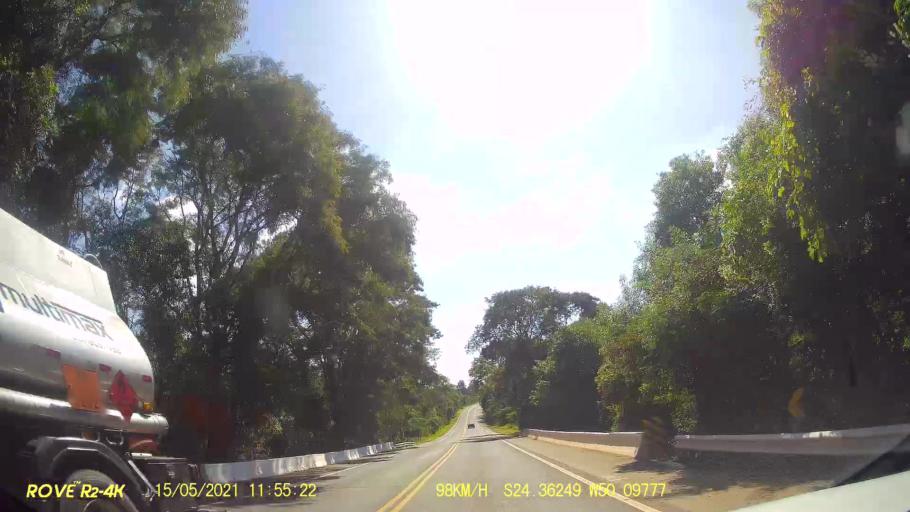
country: BR
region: Parana
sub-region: Pirai Do Sul
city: Pirai do Sul
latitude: -24.3626
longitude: -50.0977
